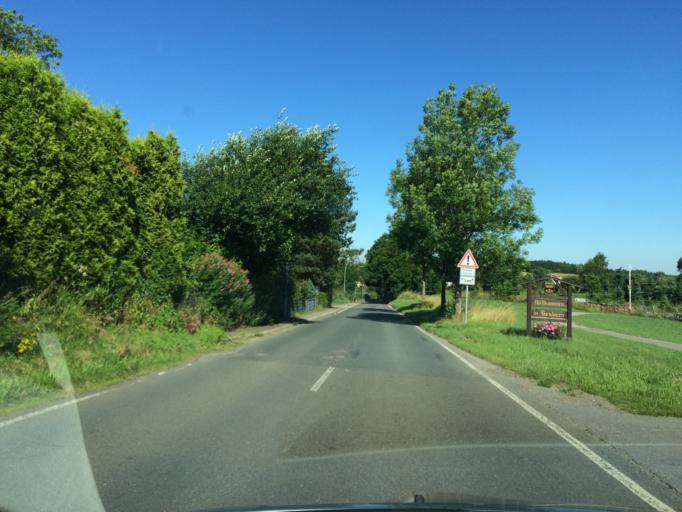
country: DE
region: North Rhine-Westphalia
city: Iserlohn
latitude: 51.3340
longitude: 7.7110
